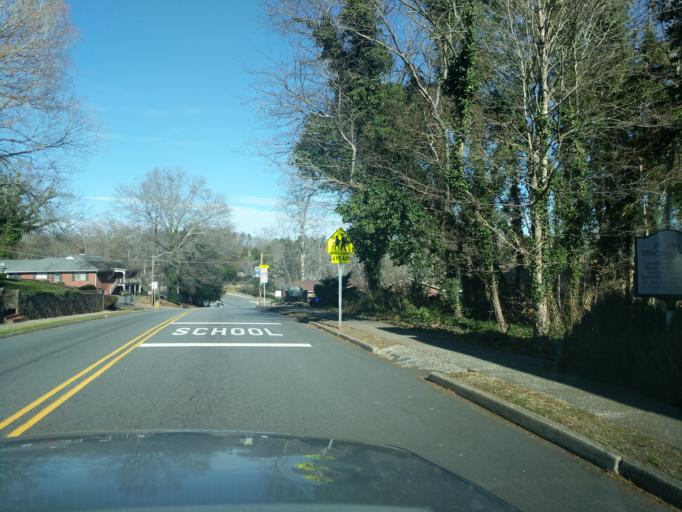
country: US
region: North Carolina
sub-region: Rutherford County
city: Rutherfordton
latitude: 35.3710
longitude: -81.9563
